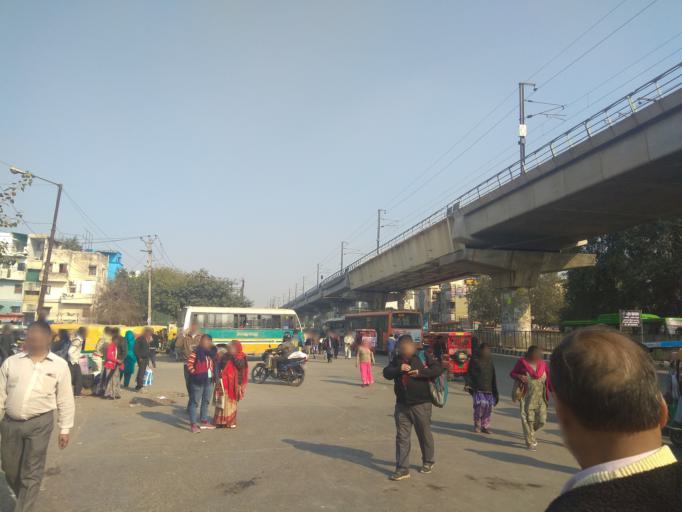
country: IN
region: NCT
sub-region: West Delhi
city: Nangloi Jat
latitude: 28.6254
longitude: 77.0663
